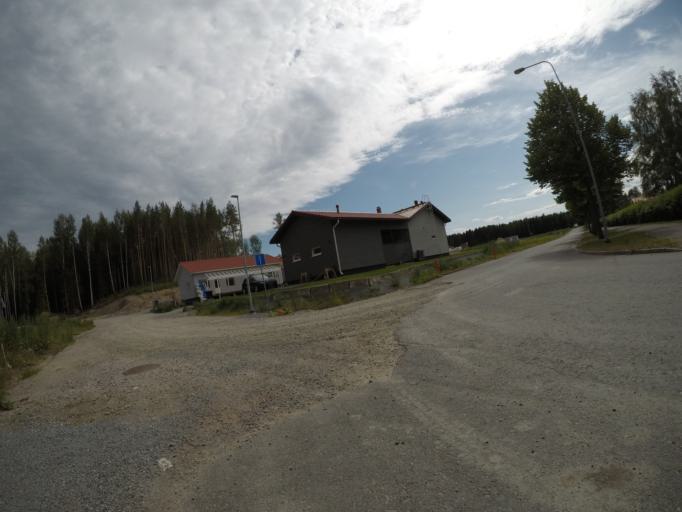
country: FI
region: Haeme
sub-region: Haemeenlinna
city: Parola
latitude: 61.0023
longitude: 24.3956
